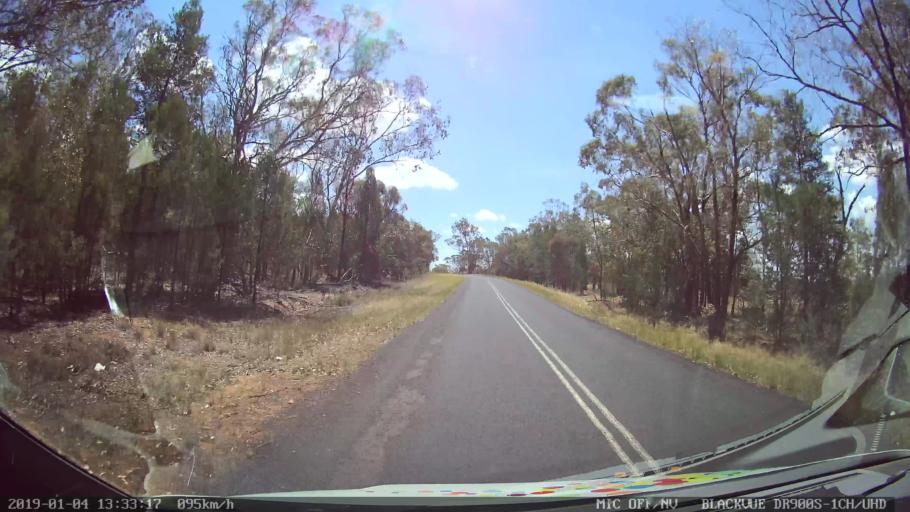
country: AU
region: New South Wales
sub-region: Dubbo Municipality
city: Eulomogo
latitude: -32.5990
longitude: 148.5438
